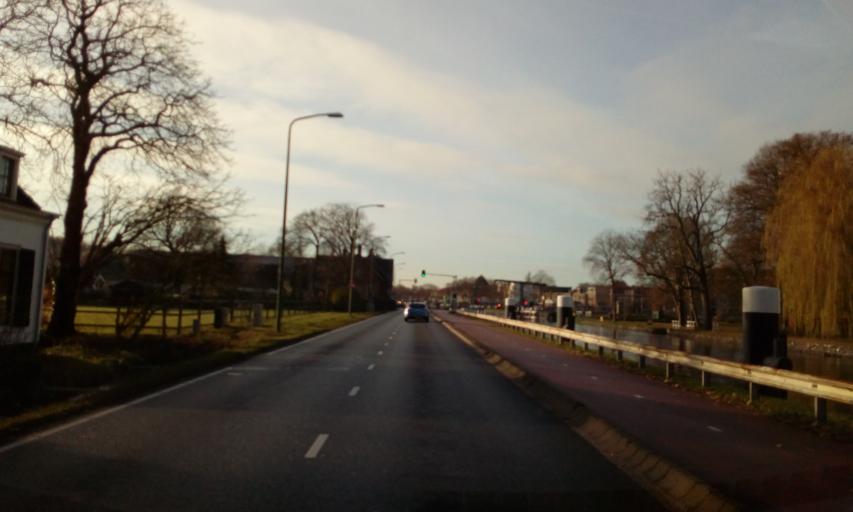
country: NL
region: South Holland
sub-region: Gemeente Leidschendam-Voorburg
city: Voorburg
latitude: 52.0575
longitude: 4.3500
